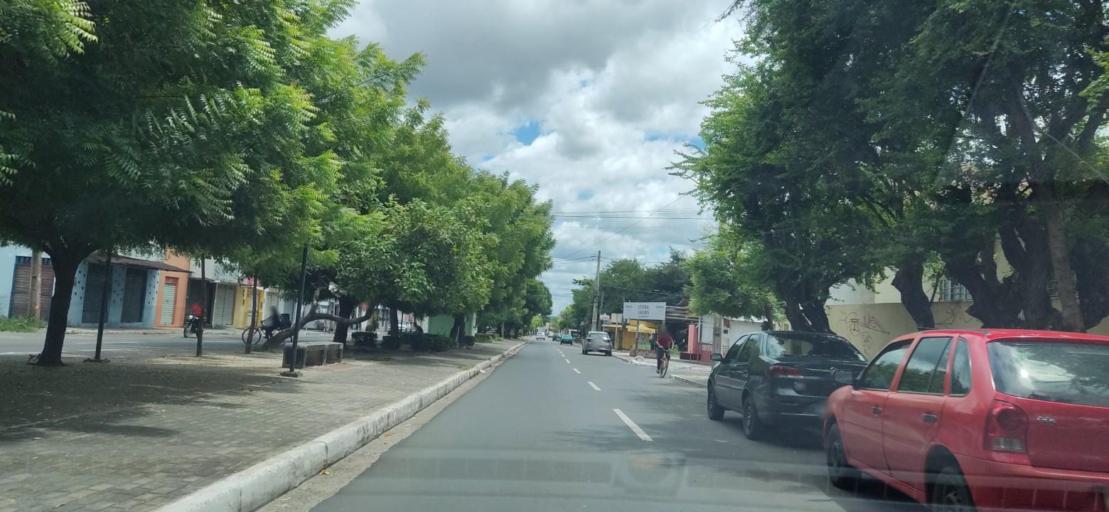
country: BR
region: Piaui
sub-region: Teresina
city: Teresina
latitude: -5.1489
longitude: -42.7823
